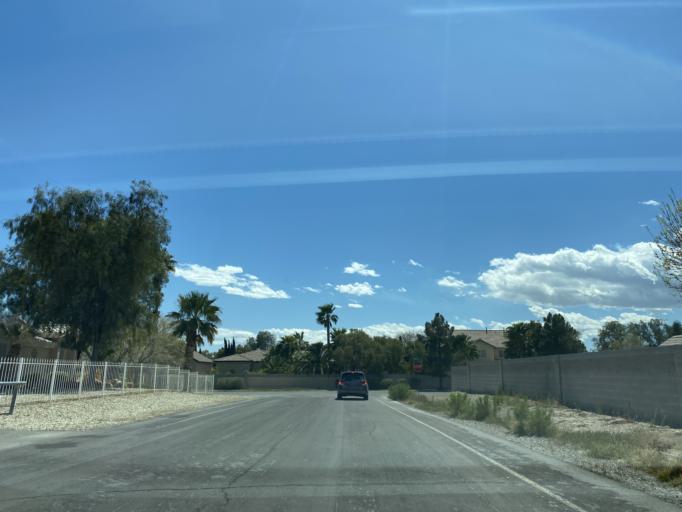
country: US
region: Nevada
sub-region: Clark County
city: North Las Vegas
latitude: 36.3095
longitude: -115.2377
